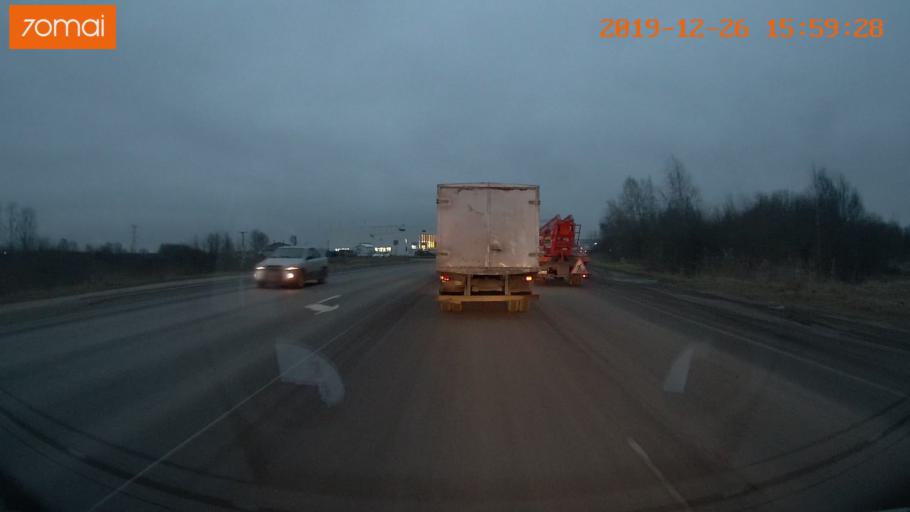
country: RU
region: Jaroslavl
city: Rybinsk
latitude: 58.0315
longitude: 38.8043
